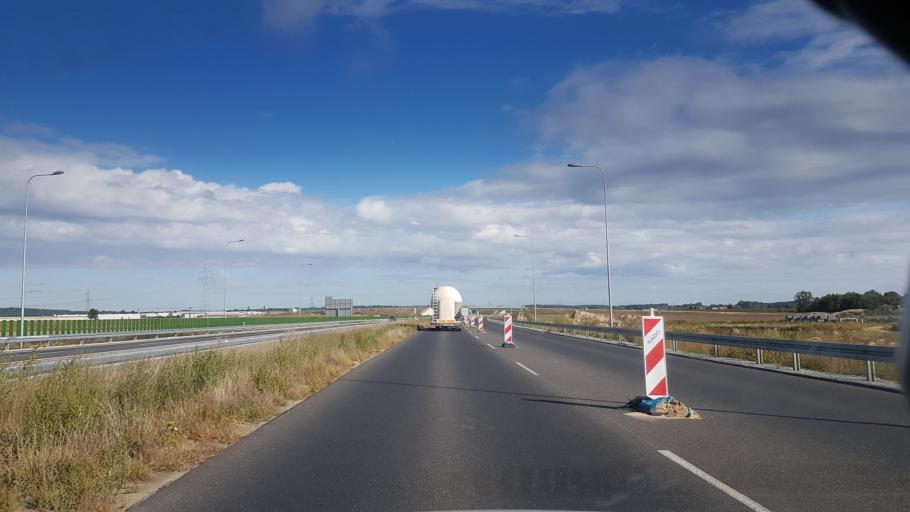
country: PL
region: Greater Poland Voivodeship
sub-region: Powiat poznanski
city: Steszew
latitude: 52.2782
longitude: 16.6693
